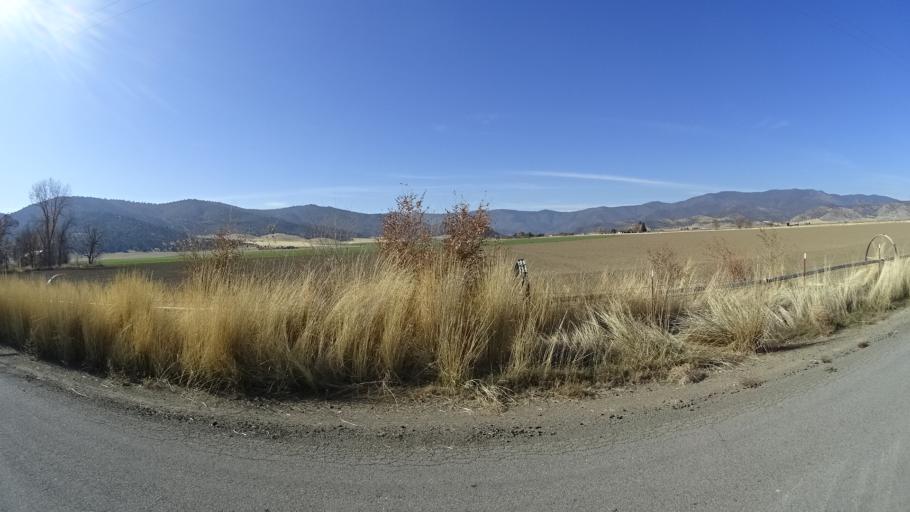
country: US
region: California
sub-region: Siskiyou County
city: Weed
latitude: 41.5360
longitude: -122.5352
